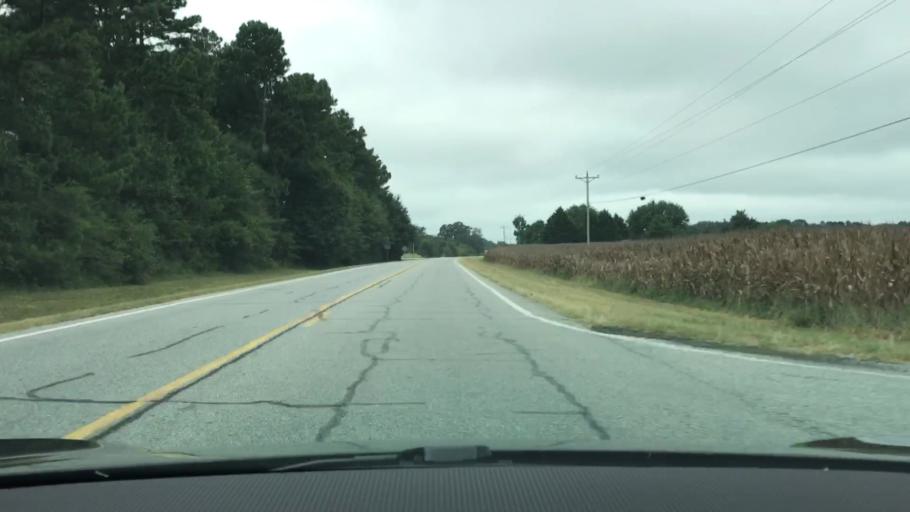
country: US
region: Georgia
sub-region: Oconee County
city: Watkinsville
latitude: 33.8136
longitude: -83.3594
